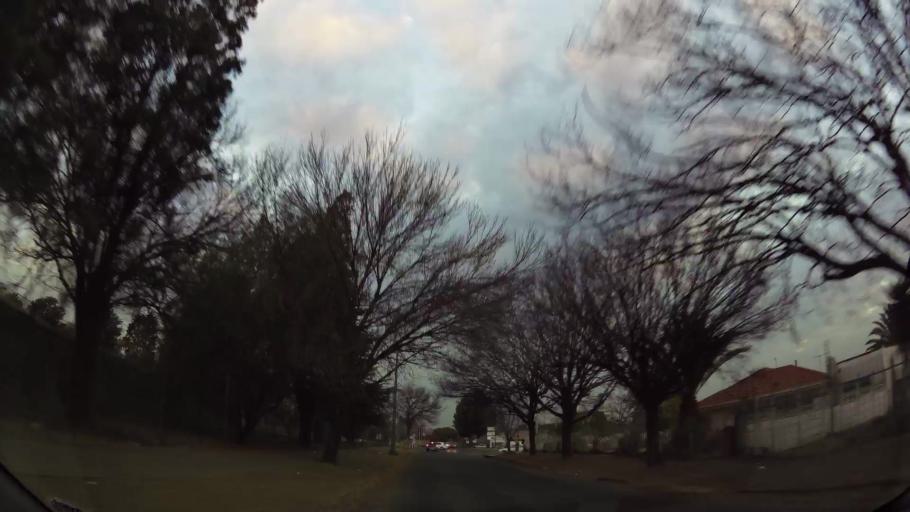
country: ZA
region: Gauteng
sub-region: Ekurhuleni Metropolitan Municipality
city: Benoni
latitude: -26.1772
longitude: 28.3093
